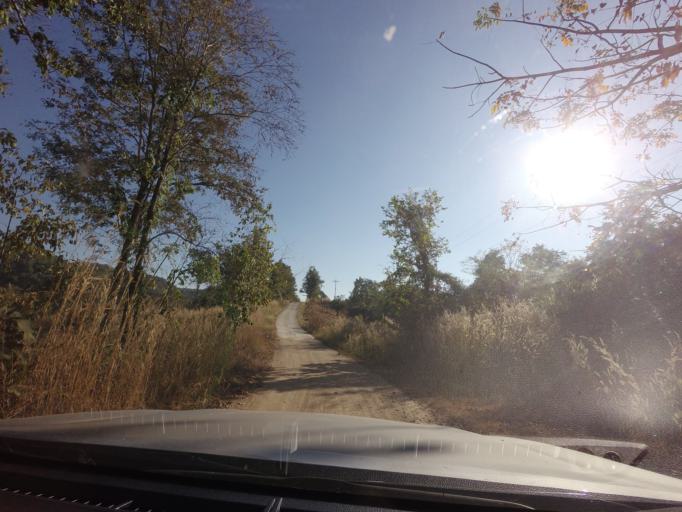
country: TH
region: Lampang
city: Chae Hom
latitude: 18.6115
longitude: 99.6419
